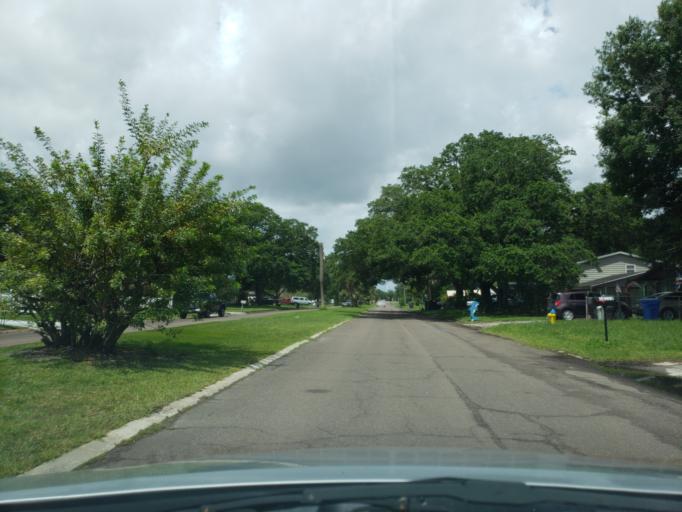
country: US
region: Florida
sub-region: Hillsborough County
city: Progress Village
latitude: 27.9251
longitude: -82.3463
